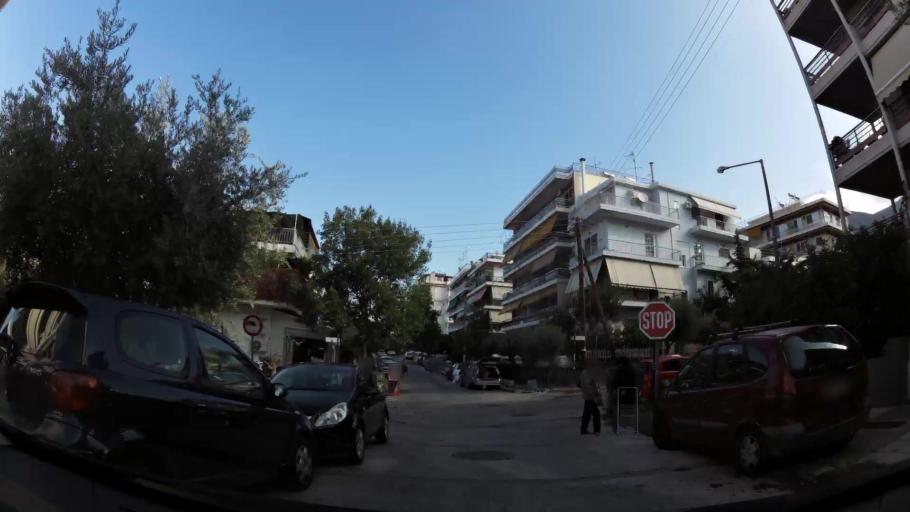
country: GR
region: Attica
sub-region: Nomarchia Athinas
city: Ilioupoli
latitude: 37.9279
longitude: 23.7600
